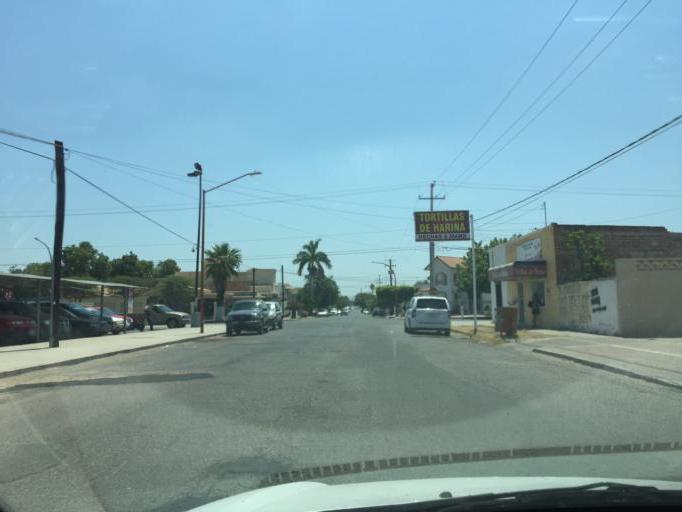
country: MX
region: Sonora
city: Navojoa
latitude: 27.0782
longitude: -109.4540
